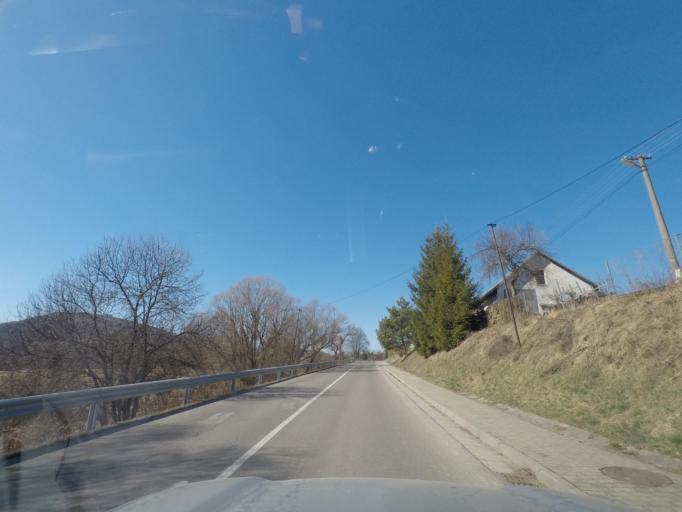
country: UA
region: Zakarpattia
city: Velykyi Bereznyi
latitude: 48.8961
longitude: 22.4004
